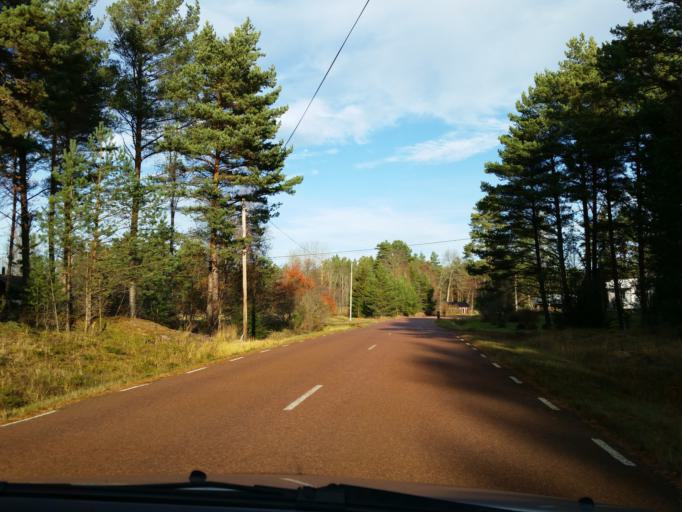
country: AX
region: Alands landsbygd
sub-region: Saltvik
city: Saltvik
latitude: 60.3532
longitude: 20.0952
